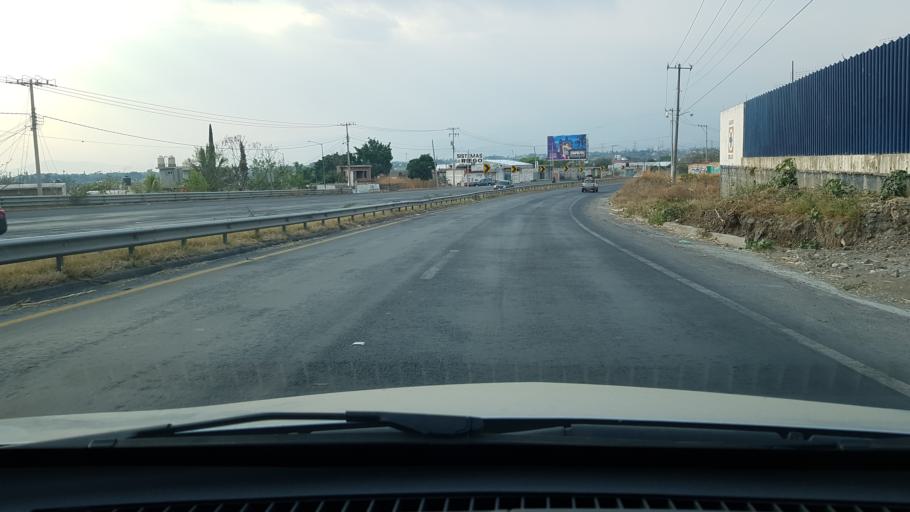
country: MX
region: Morelos
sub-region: Yecapixtla
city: Juan Morales
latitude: 18.8225
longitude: -98.9214
